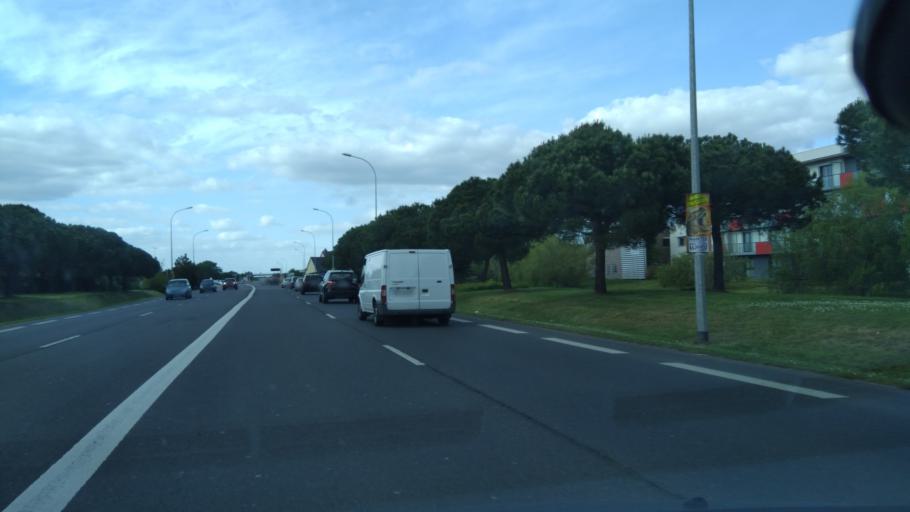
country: FR
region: Pays de la Loire
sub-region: Departement de la Loire-Atlantique
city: Saint-Nazaire
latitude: 47.2965
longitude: -2.2077
